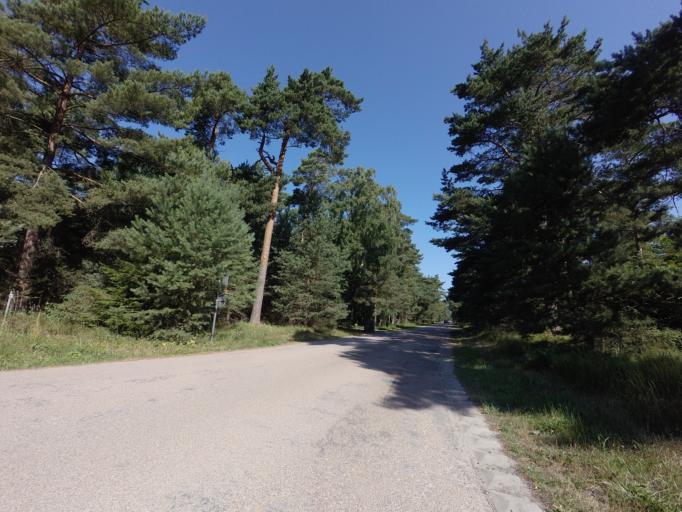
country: SE
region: Skane
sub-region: Vellinge Kommun
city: Ljunghusen
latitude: 55.3933
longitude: 12.9241
